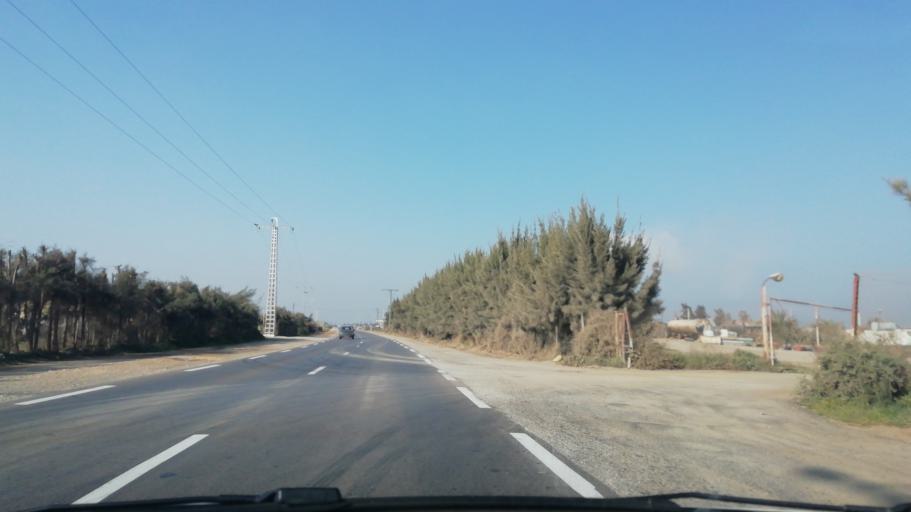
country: DZ
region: Mostaganem
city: Mostaganem
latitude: 35.7516
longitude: 0.0374
